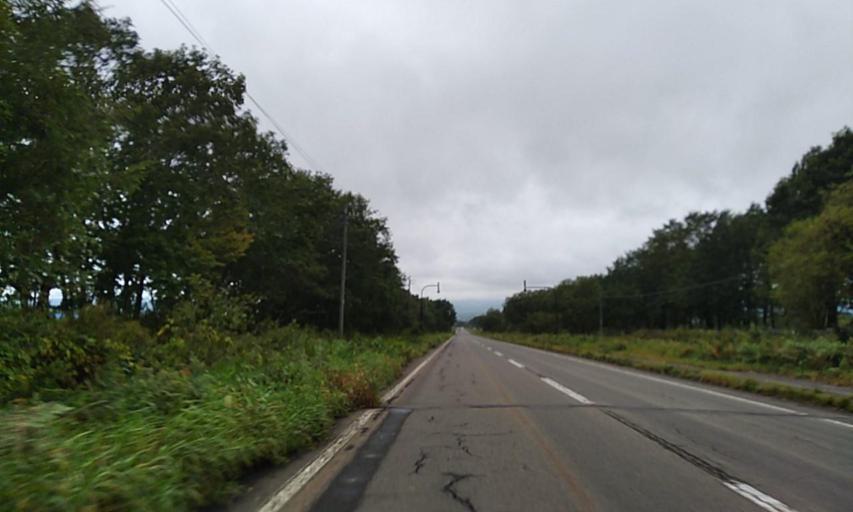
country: JP
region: Hokkaido
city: Bihoro
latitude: 43.5200
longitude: 144.4823
